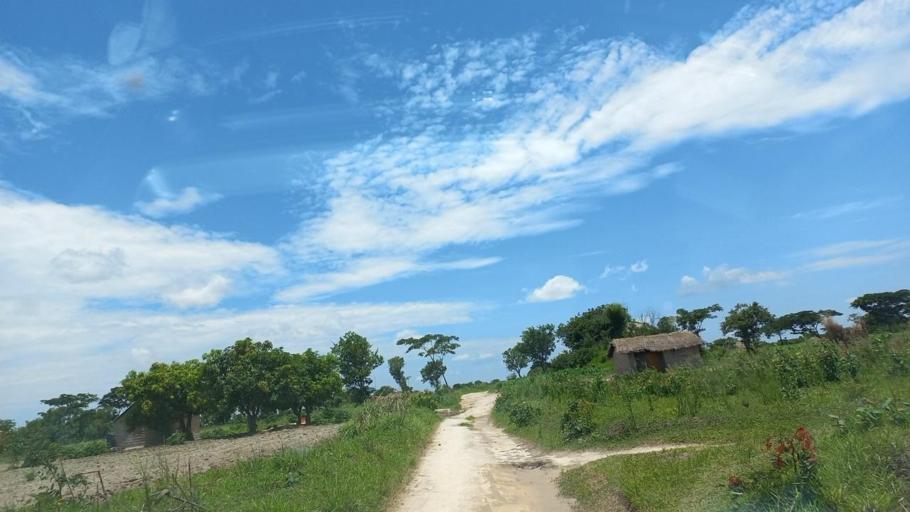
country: ZM
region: Copperbelt
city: Ndola
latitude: -12.8686
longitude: 28.4359
